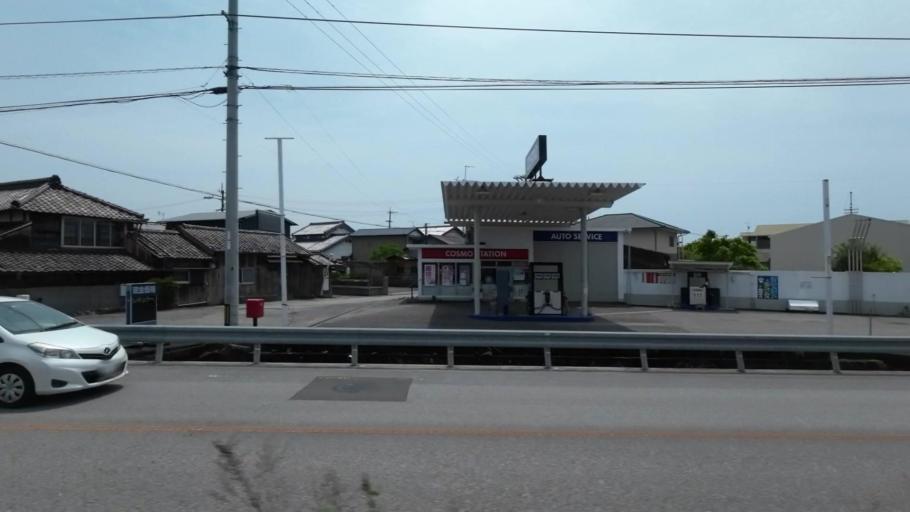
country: JP
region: Kochi
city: Kochi-shi
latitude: 33.5884
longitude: 133.6583
